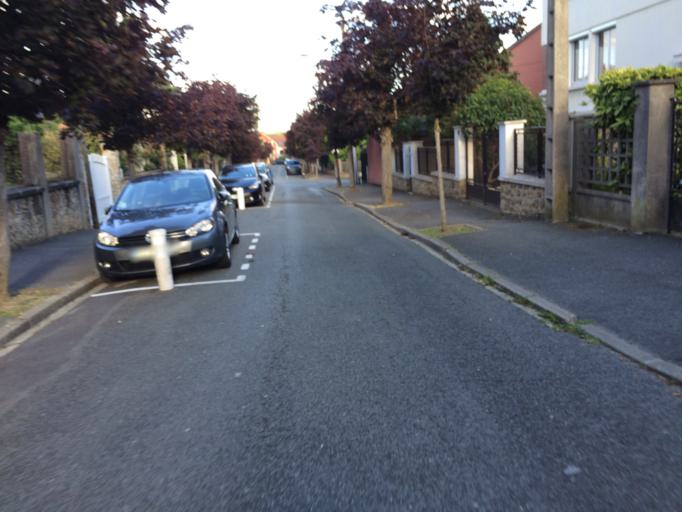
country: FR
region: Ile-de-France
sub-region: Departement de l'Essonne
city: Orsay
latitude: 48.7050
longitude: 2.2123
